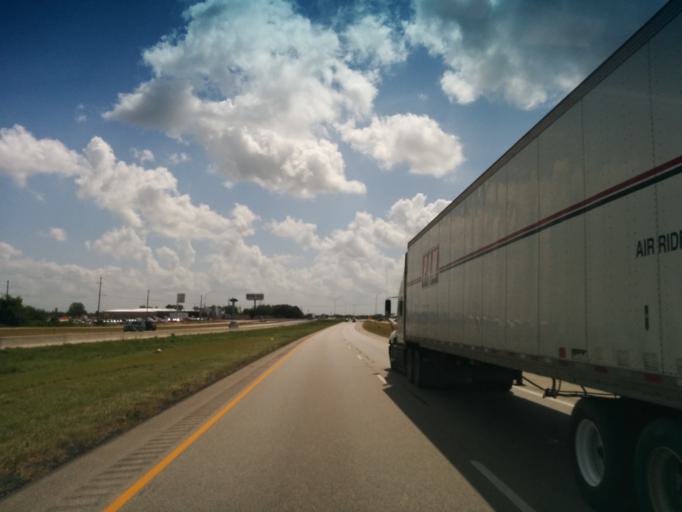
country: US
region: Texas
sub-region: Austin County
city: Sealy
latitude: 29.7744
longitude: -96.1303
